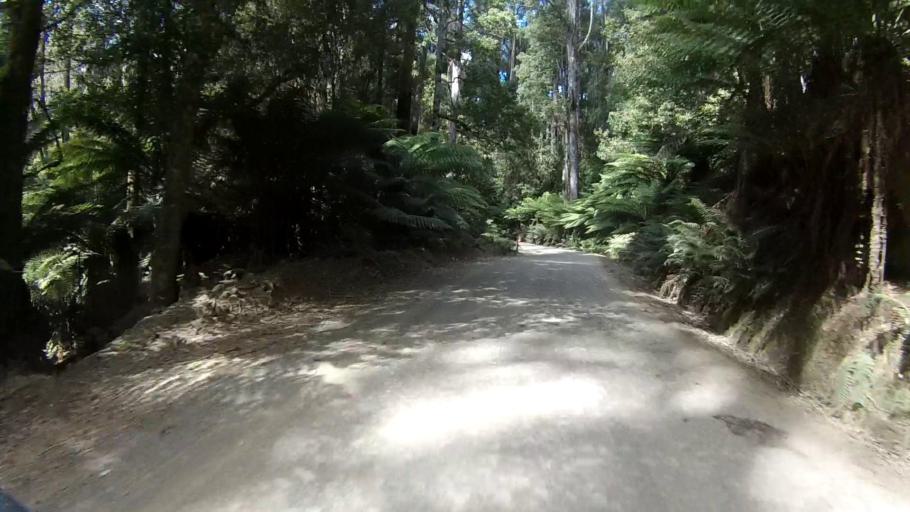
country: AU
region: Tasmania
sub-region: Derwent Valley
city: New Norfolk
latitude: -42.6791
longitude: 146.6974
